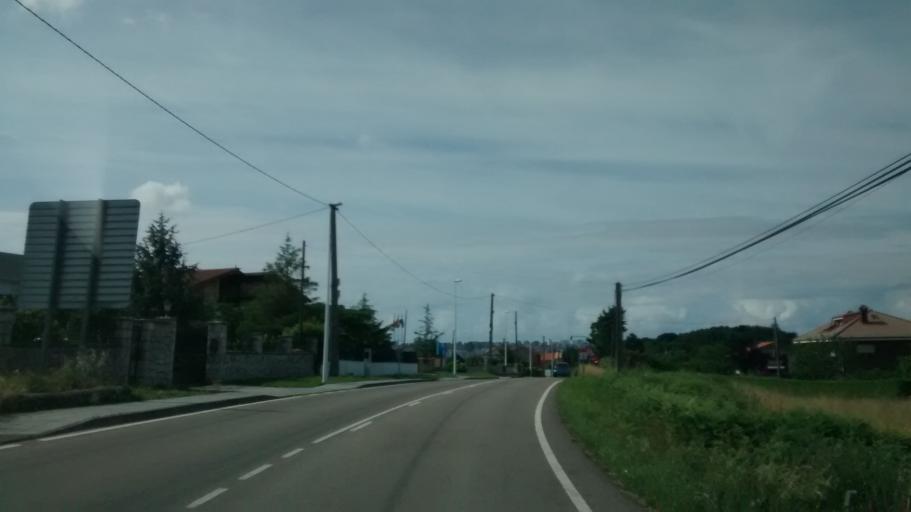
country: ES
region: Cantabria
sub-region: Provincia de Cantabria
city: Santander
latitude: 43.4288
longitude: -3.7721
